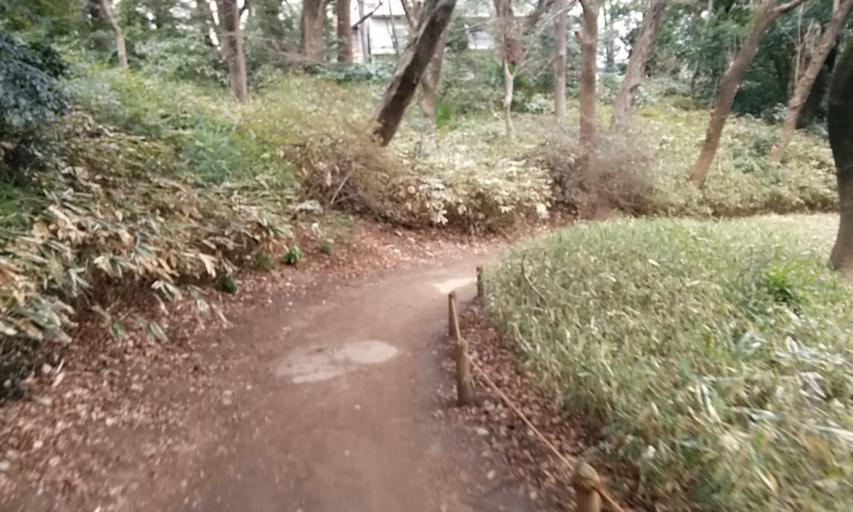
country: JP
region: Tokyo
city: Tokyo
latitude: 35.7345
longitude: 139.7465
